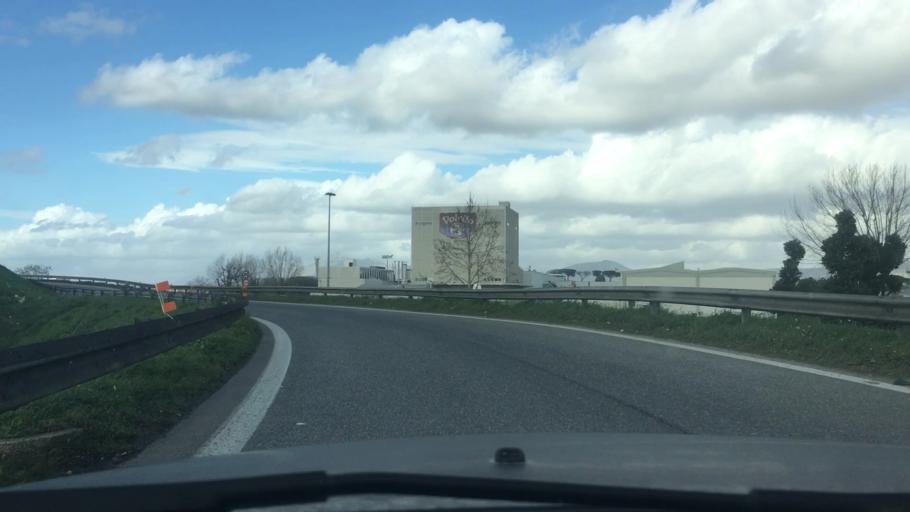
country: IT
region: Campania
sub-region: Provincia di Caserta
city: San Marco Evangelista
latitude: 41.0191
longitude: 14.3241
